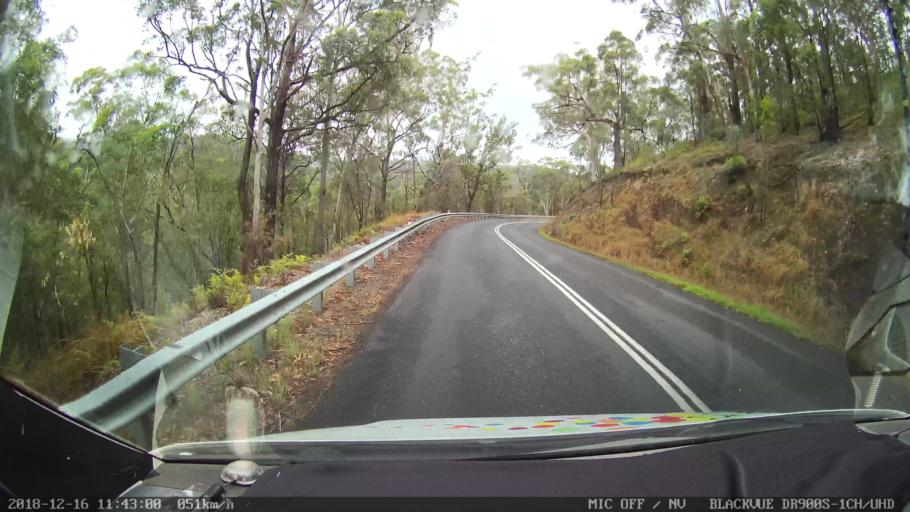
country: AU
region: New South Wales
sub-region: Tenterfield Municipality
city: Carrolls Creek
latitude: -28.9488
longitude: 152.2153
